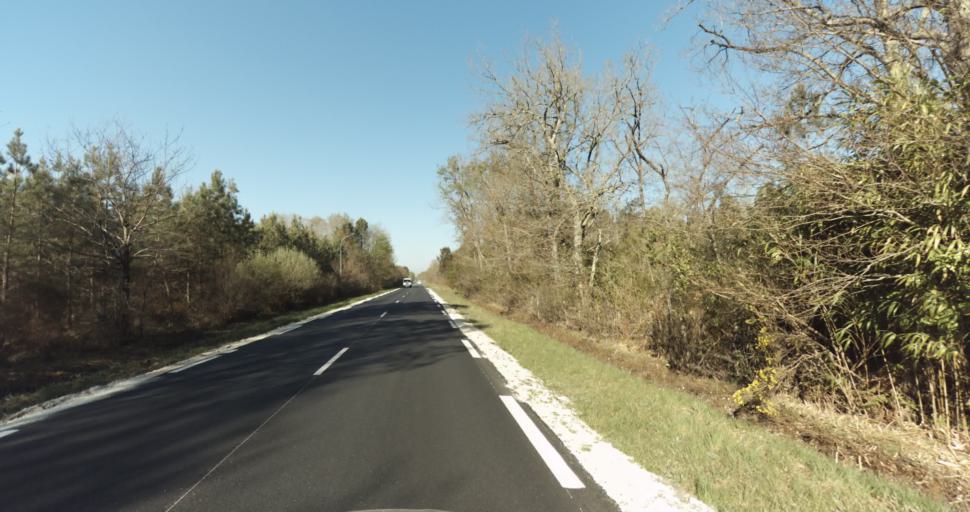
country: FR
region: Aquitaine
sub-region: Departement de la Gironde
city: Martignas-sur-Jalle
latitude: 44.7949
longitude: -0.8571
